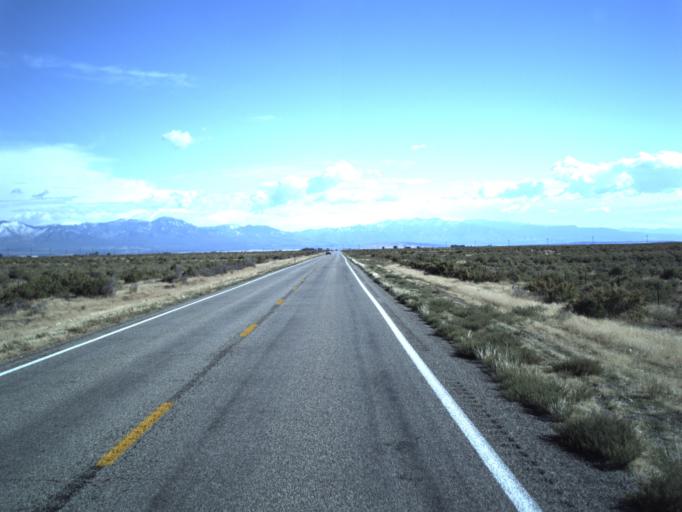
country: US
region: Utah
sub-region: Millard County
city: Delta
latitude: 39.2454
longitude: -112.4362
